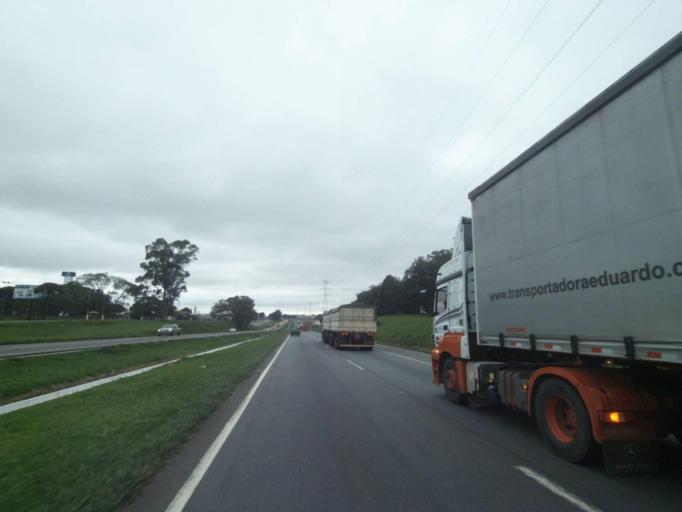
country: BR
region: Parana
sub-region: Curitiba
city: Curitiba
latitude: -25.4581
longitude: -49.3600
